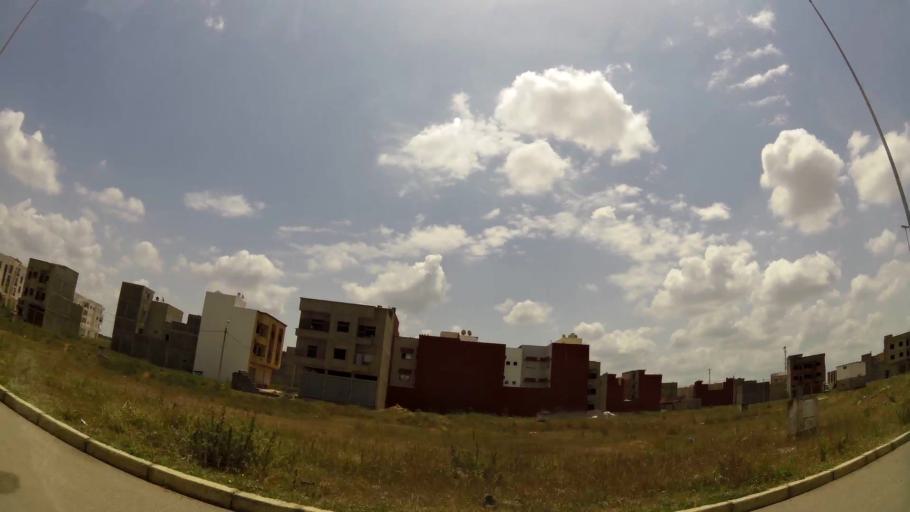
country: MA
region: Rabat-Sale-Zemmour-Zaer
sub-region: Khemisset
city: Tiflet
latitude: 34.0102
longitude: -6.5221
